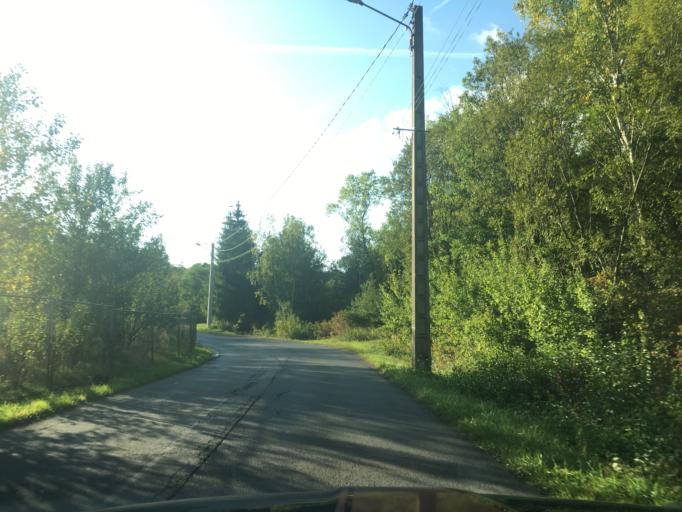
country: FR
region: Lorraine
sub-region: Departement de Meurthe-et-Moselle
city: Hussigny-Godbrange
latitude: 49.4983
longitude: 5.8687
